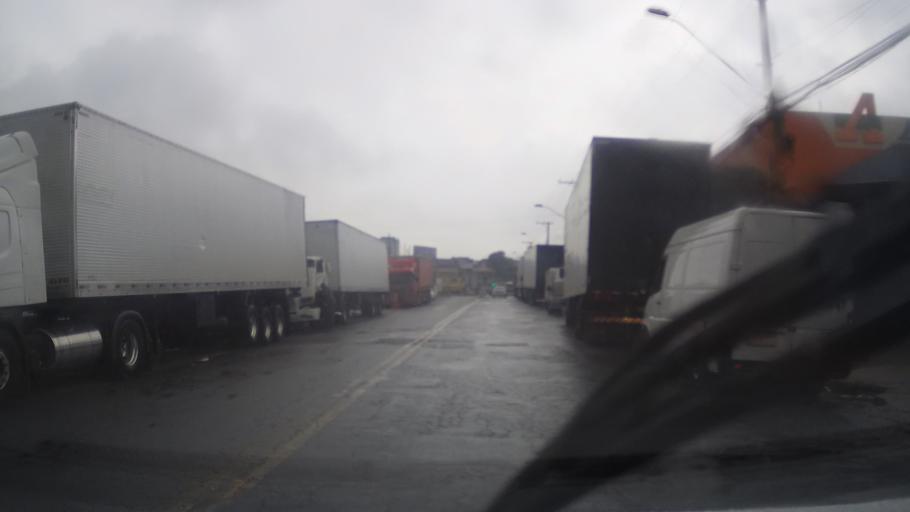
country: BR
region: Sao Paulo
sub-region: Guarulhos
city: Guarulhos
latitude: -23.4397
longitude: -46.5058
